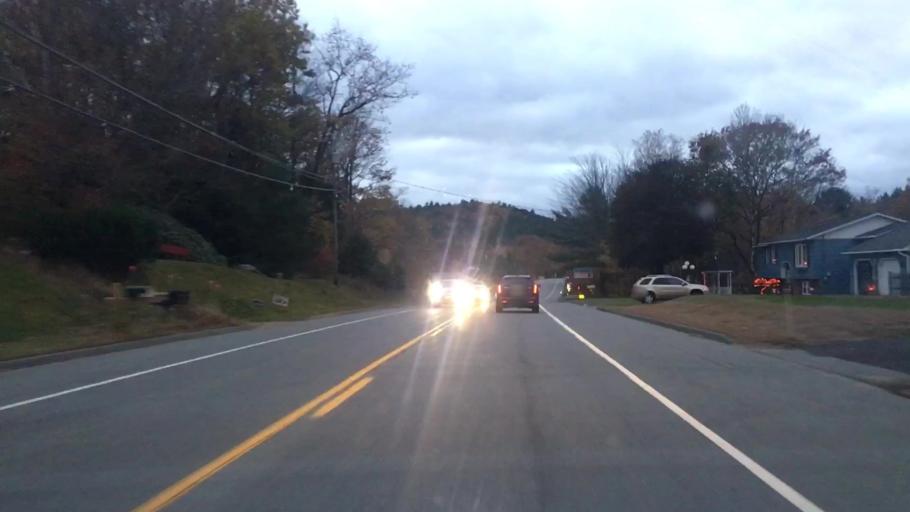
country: US
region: Maine
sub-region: Oxford County
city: Dixfield
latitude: 44.5240
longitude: -70.4558
